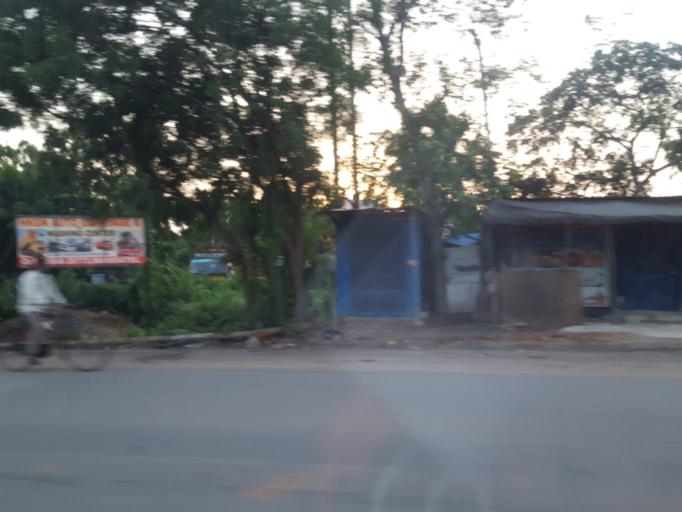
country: IN
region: Telangana
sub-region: Medak
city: Serilingampalle
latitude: 17.5313
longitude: 78.3562
